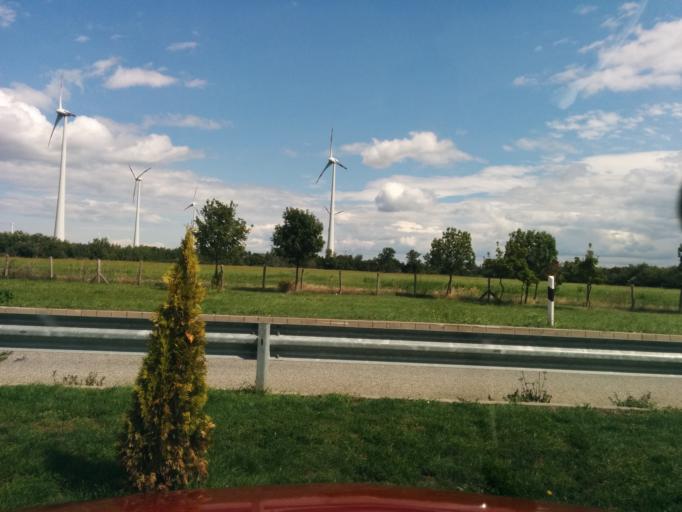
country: HU
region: Gyor-Moson-Sopron
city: Mosonmagyarovar
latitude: 47.8718
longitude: 17.2176
